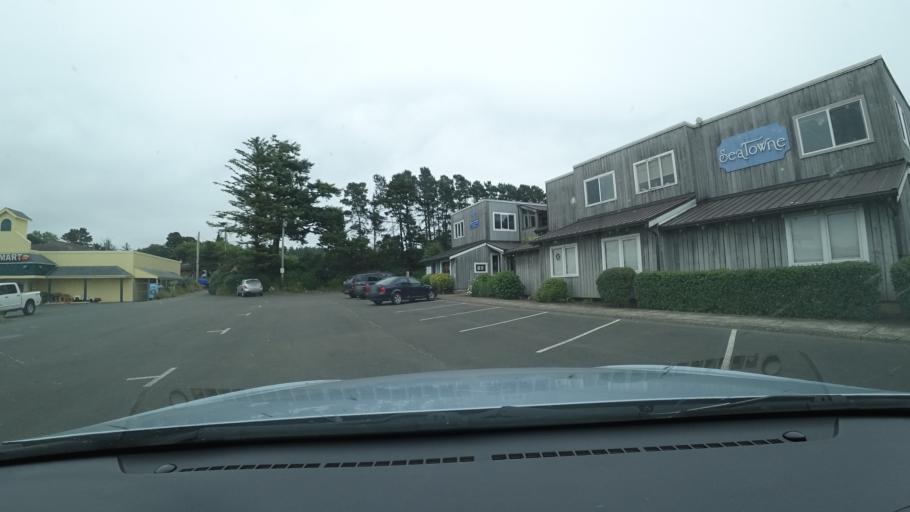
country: US
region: Oregon
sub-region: Lincoln County
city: Newport
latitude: 44.6500
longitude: -124.0526
